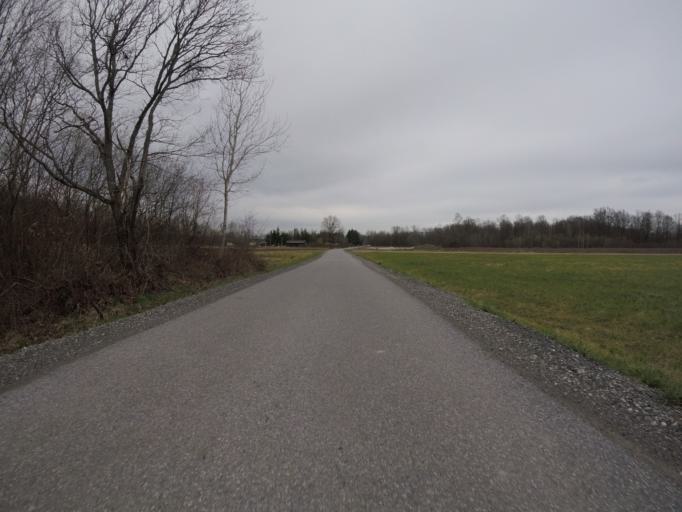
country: HR
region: Grad Zagreb
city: Strmec
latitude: 45.6701
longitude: 15.8864
